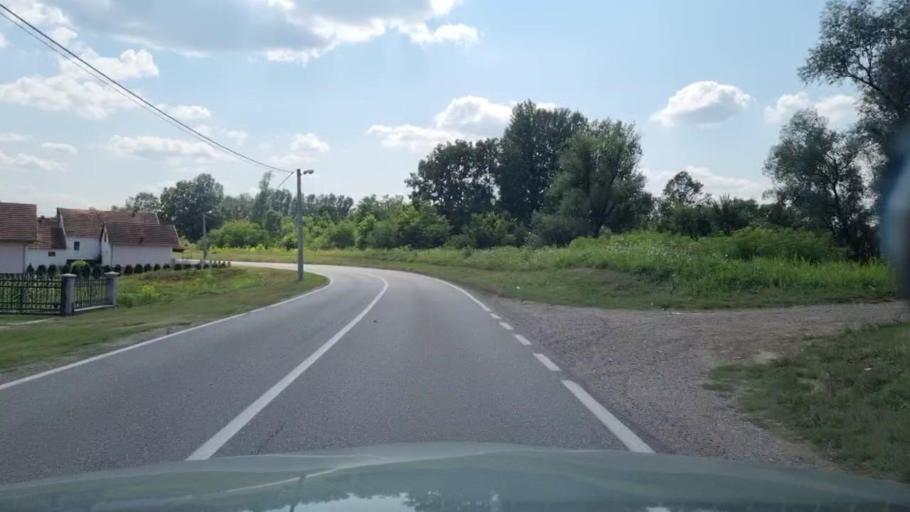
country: HR
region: Brodsko-Posavska
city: Krusevica
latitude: 45.0608
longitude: 18.5515
